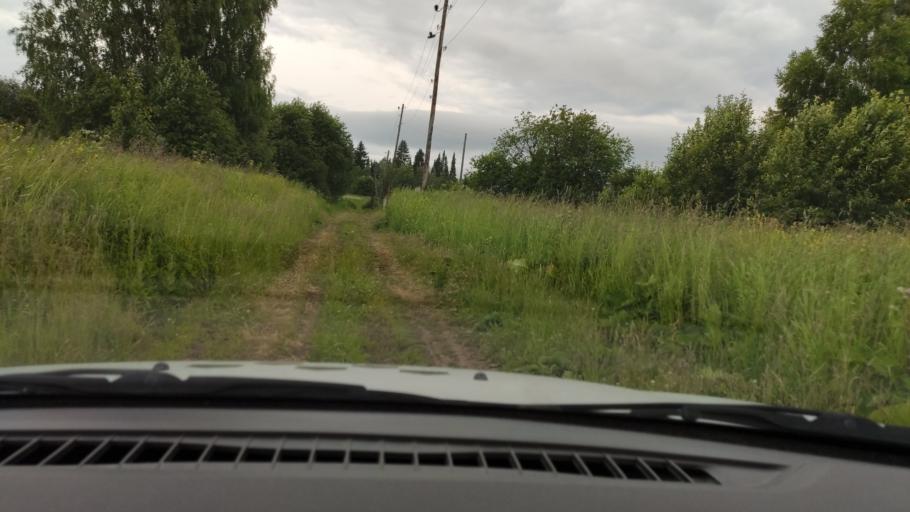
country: RU
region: Perm
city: Orda
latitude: 57.2934
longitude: 56.5791
